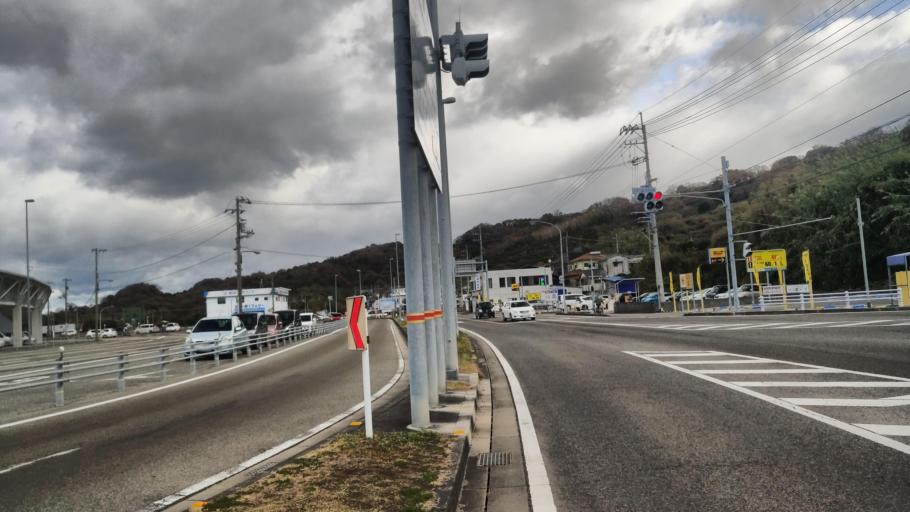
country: JP
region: Ehime
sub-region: Shikoku-chuo Shi
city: Matsuyama
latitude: 33.8889
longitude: 132.7054
